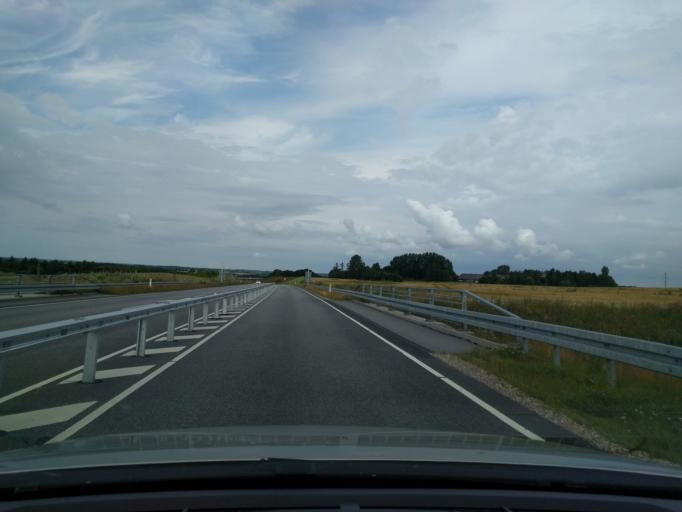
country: DK
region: Zealand
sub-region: Naestved Kommune
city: Fensmark
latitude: 55.2623
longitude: 11.7851
